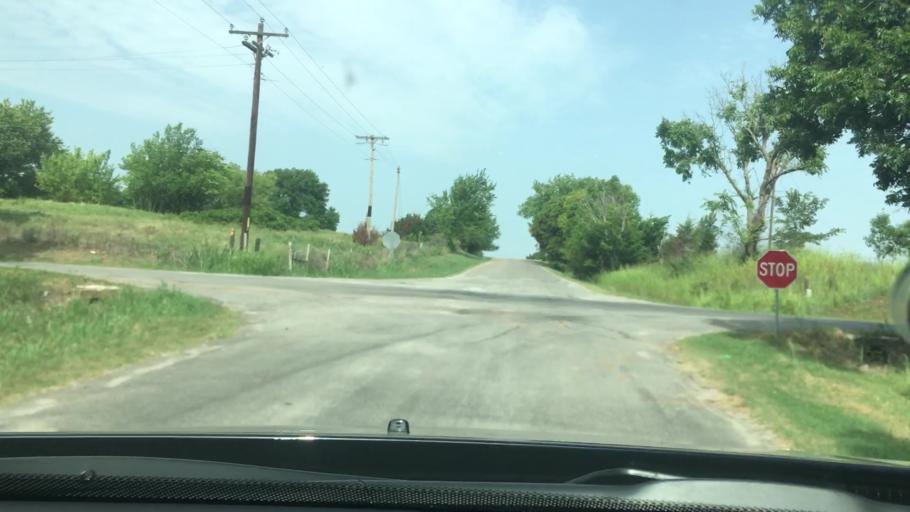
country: US
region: Oklahoma
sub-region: Garvin County
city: Pauls Valley
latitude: 34.7969
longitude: -97.1952
